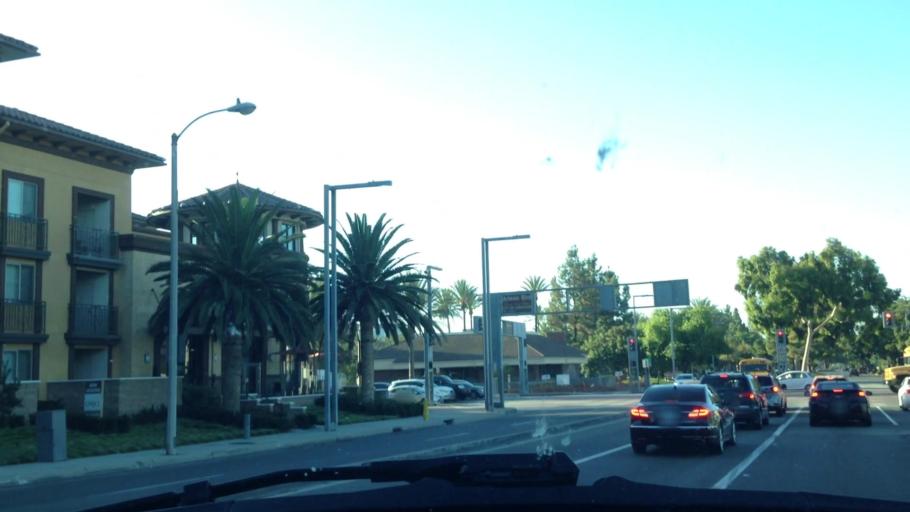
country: US
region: California
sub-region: Los Angeles County
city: Cerritos
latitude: 33.8738
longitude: -118.0639
